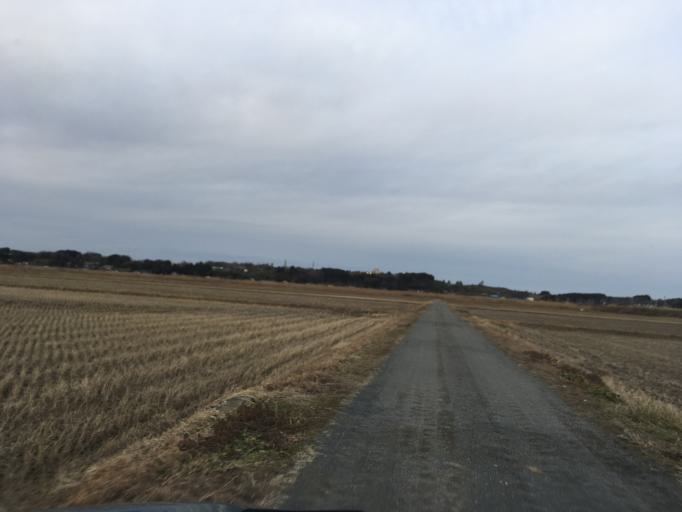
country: JP
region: Miyagi
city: Kogota
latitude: 38.6414
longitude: 141.0677
